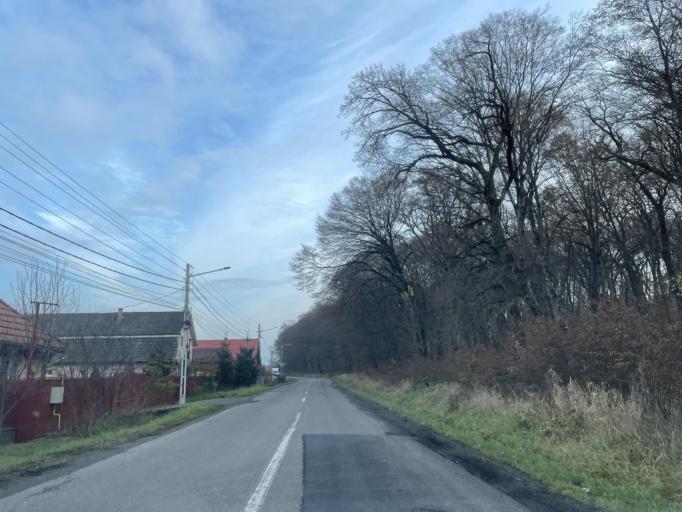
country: RO
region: Mures
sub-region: Comuna Solovastru
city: Solovastru
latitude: 46.7758
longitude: 24.7465
